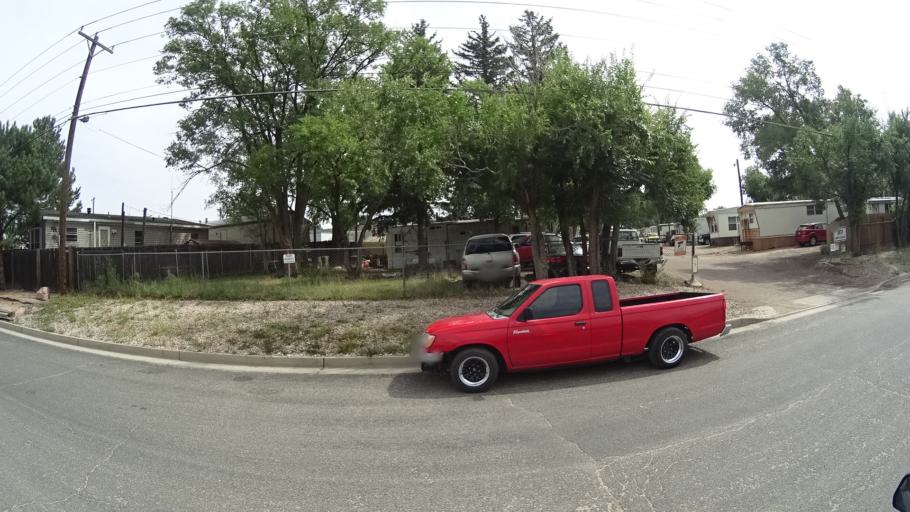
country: US
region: Colorado
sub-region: El Paso County
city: Colorado Springs
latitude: 38.8878
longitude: -104.8227
